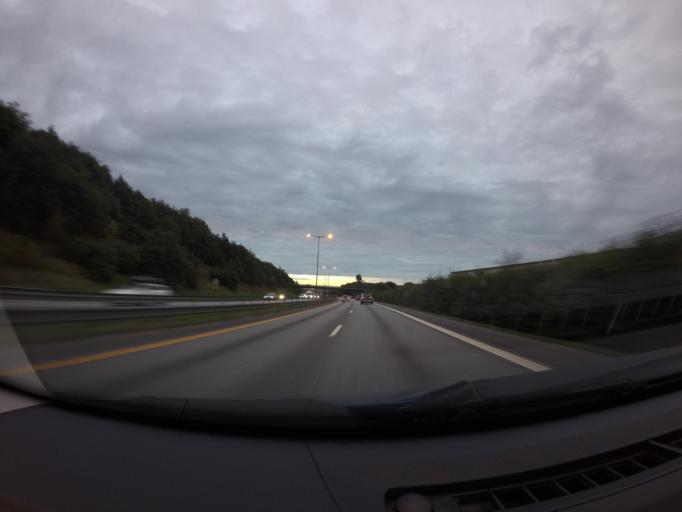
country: NO
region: Rogaland
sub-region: Sandnes
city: Sandnes
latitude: 58.8961
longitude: 5.7100
